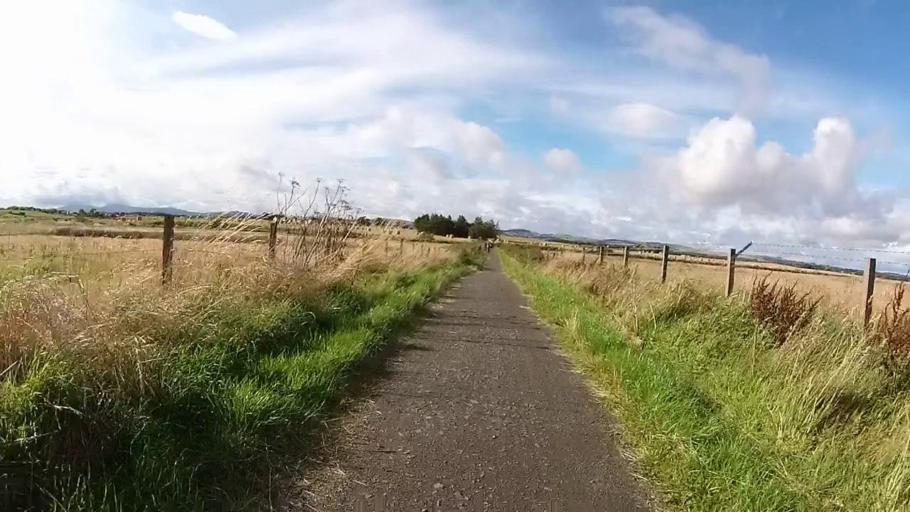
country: GB
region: Scotland
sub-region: Perth and Kinross
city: Kinross
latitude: 56.1778
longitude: -3.3868
